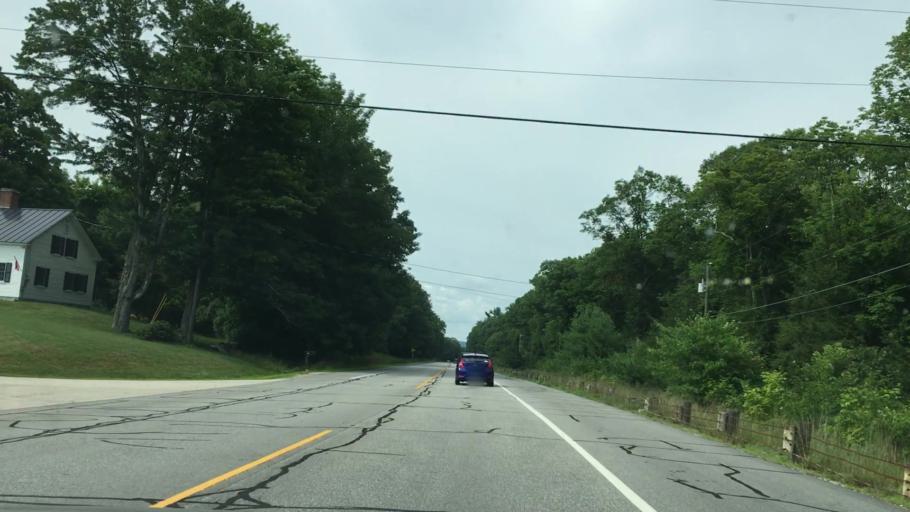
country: US
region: New Hampshire
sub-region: Hillsborough County
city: Antrim
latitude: 43.0677
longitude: -71.9156
